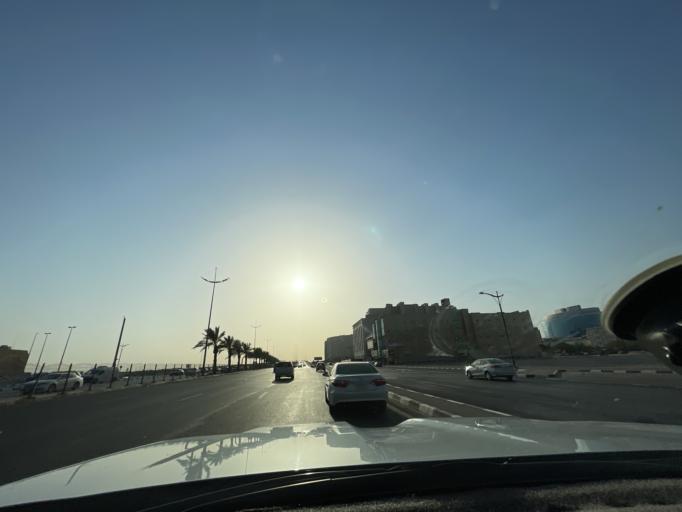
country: SA
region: Eastern Province
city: Khobar
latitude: 26.2880
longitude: 50.1843
